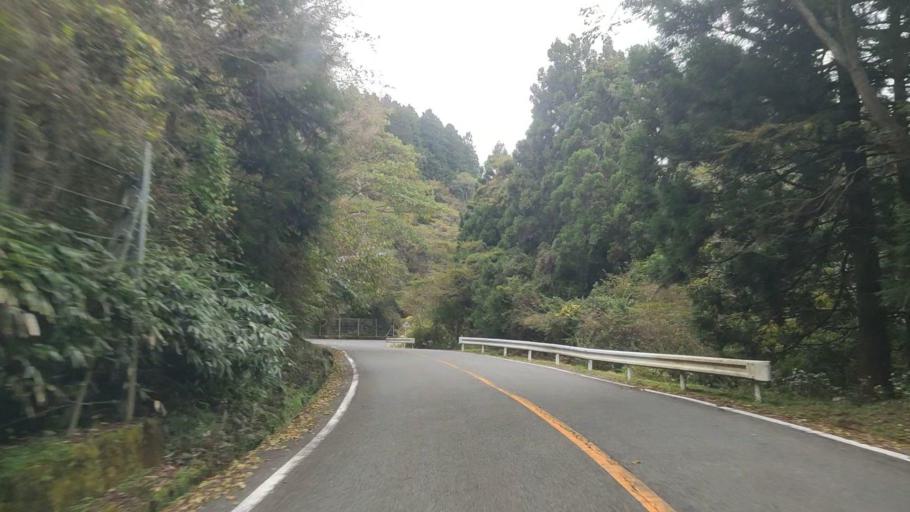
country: JP
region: Shizuoka
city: Heda
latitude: 34.9271
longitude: 138.8405
